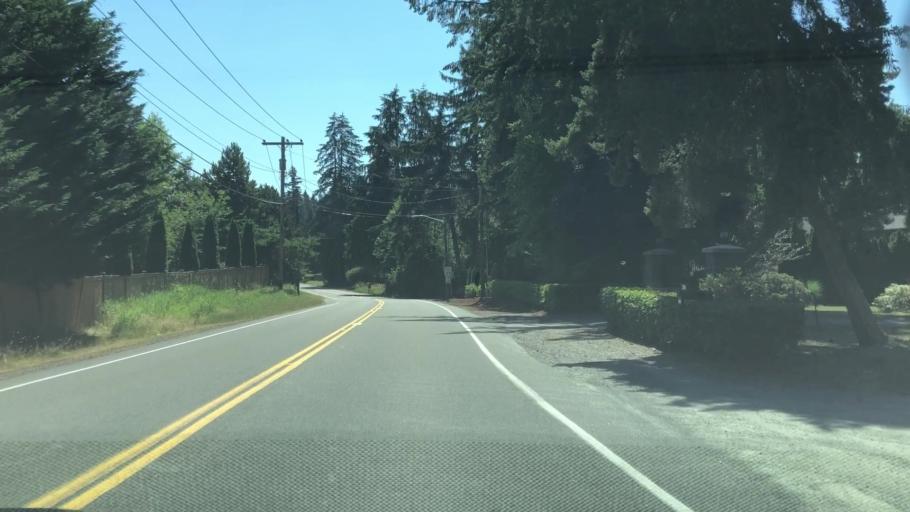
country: US
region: Washington
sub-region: King County
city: Cottage Lake
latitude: 47.7611
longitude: -122.1117
